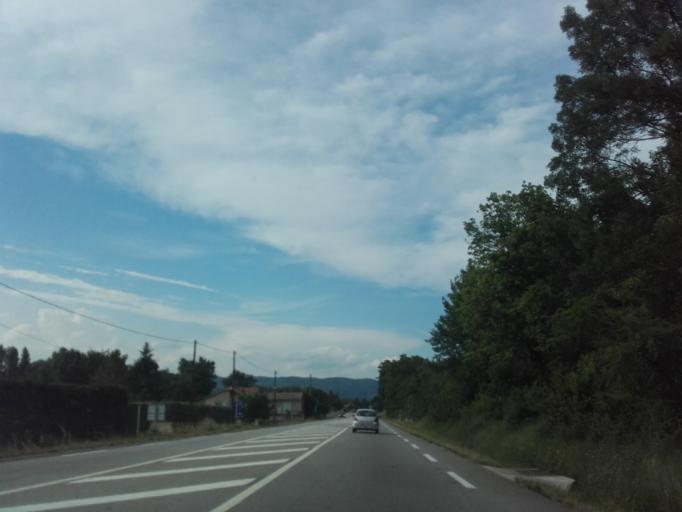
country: FR
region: Rhone-Alpes
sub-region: Departement de la Drome
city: Ancone
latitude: 44.5865
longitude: 4.7523
